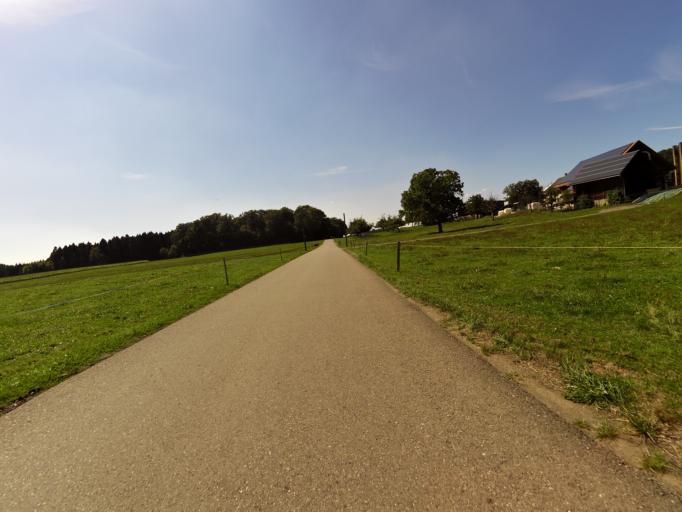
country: CH
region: Thurgau
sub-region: Weinfelden District
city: Maerstetten-Dorf
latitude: 47.6291
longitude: 9.0867
